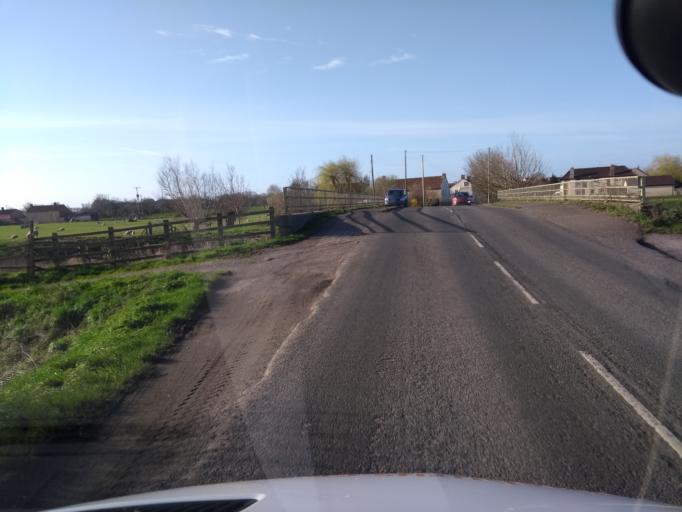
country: GB
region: England
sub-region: Somerset
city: Wedmore
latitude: 51.1807
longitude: -2.8059
